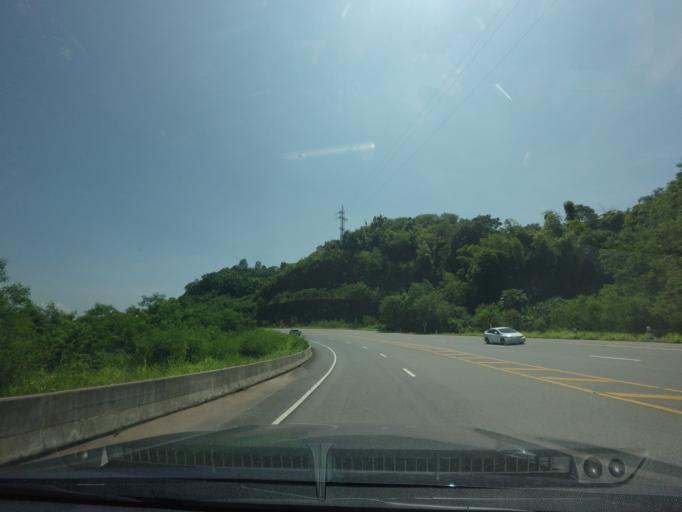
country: TH
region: Phetchabun
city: Lom Sak
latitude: 16.7806
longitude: 101.1048
